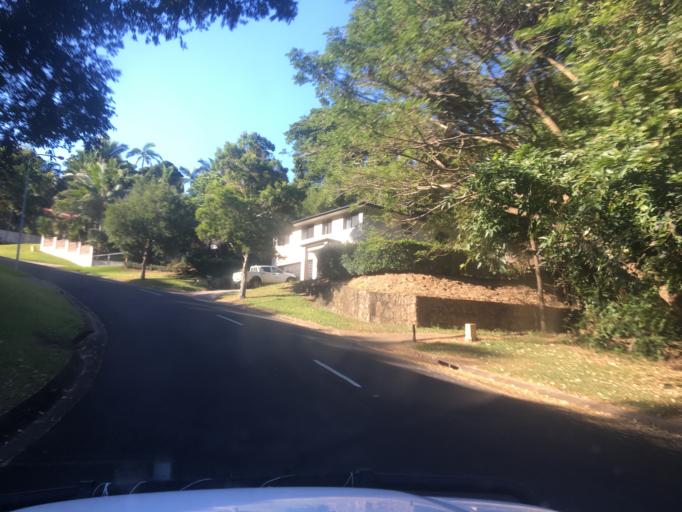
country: AU
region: Queensland
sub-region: Cairns
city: Woree
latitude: -16.9336
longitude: 145.7240
